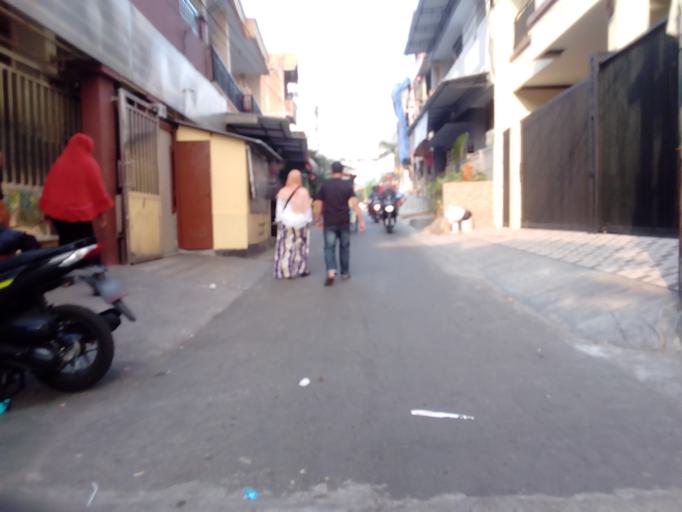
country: ID
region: Jakarta Raya
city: Jakarta
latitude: -6.1947
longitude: 106.8113
